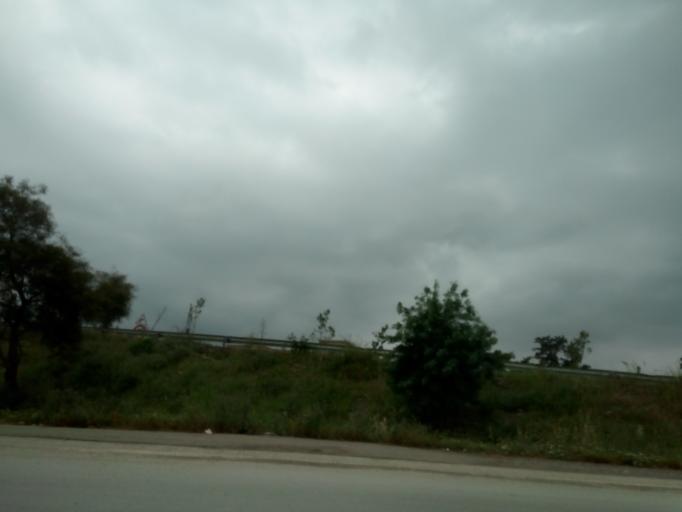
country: DZ
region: Blida
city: Chiffa
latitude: 36.4586
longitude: 2.7473
